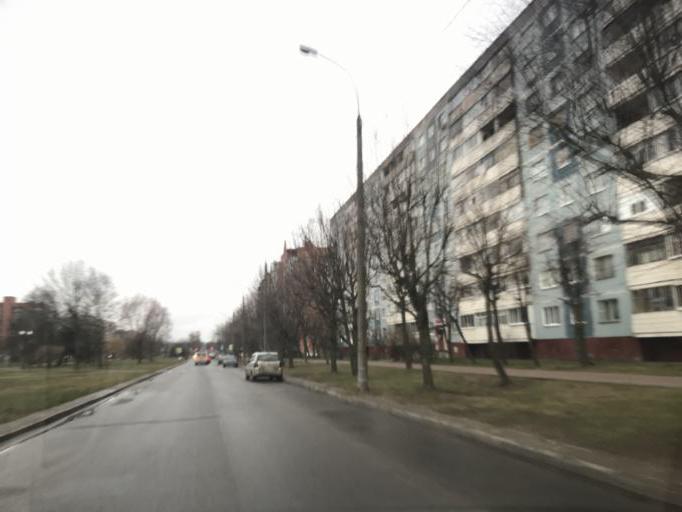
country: BY
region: Mogilev
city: Mahilyow
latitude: 53.8721
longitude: 30.3358
